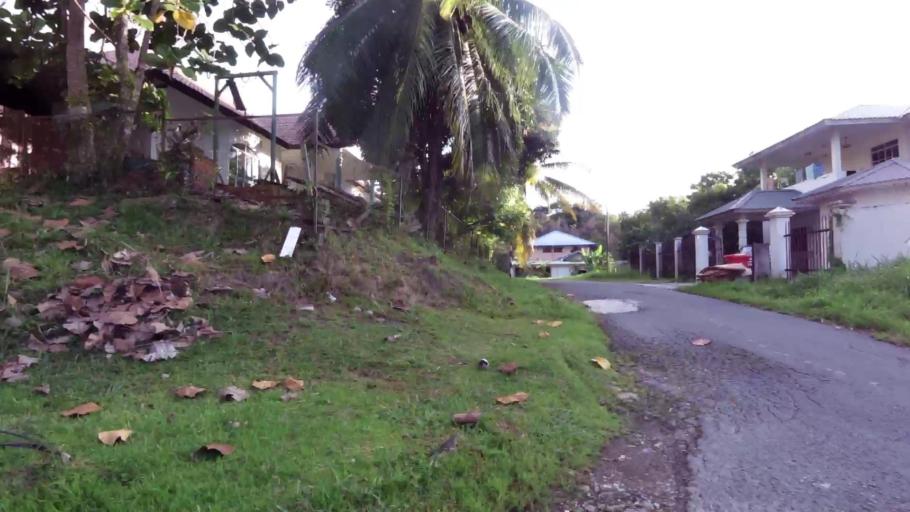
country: BN
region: Brunei and Muara
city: Bandar Seri Begawan
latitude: 4.9771
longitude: 114.9912
